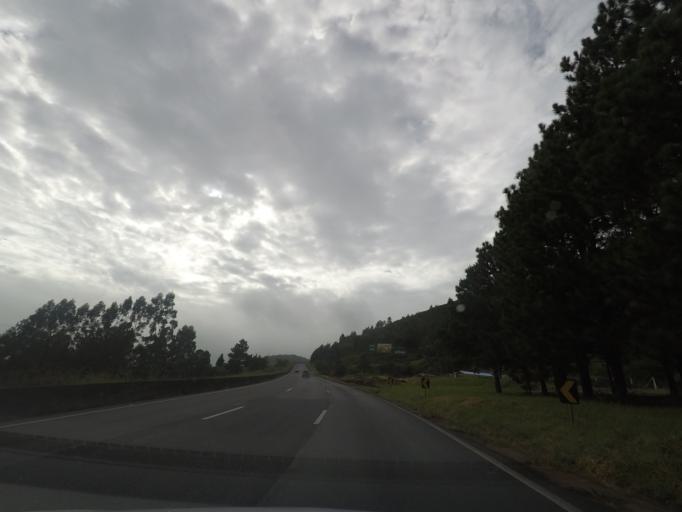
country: BR
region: Parana
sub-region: Campina Grande Do Sul
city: Campina Grande do Sul
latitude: -25.1091
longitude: -48.8277
